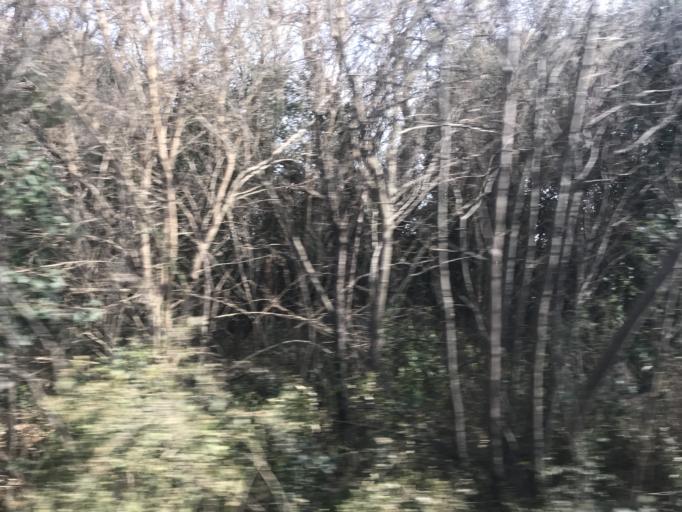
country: AR
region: Cordoba
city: Laguna Larga
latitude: -31.7905
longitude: -63.7914
